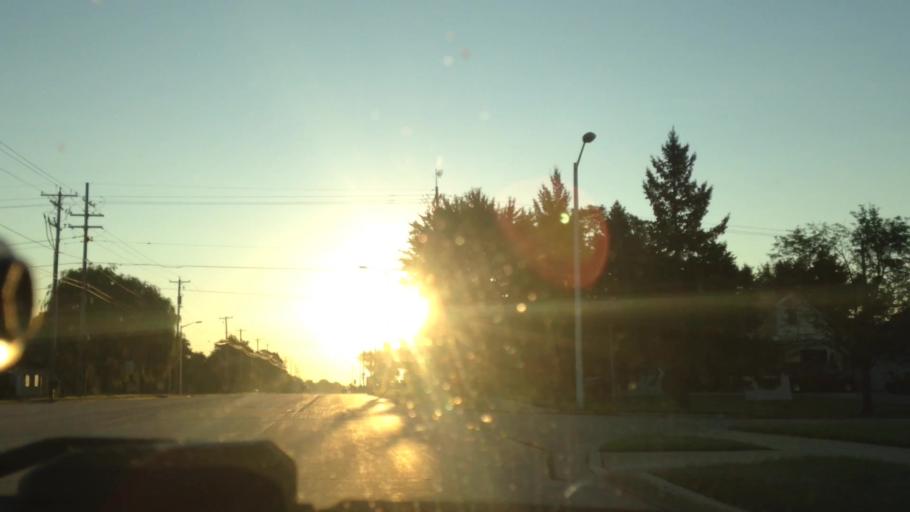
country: US
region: Wisconsin
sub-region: Washington County
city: West Bend
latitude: 43.4267
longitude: -88.1521
